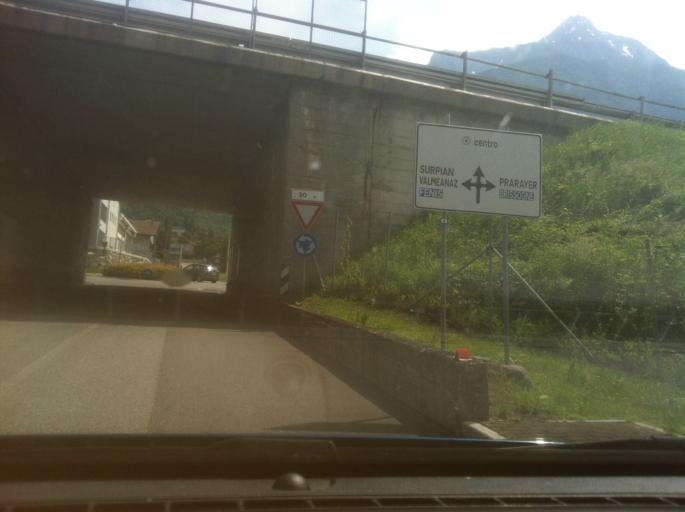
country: IT
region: Aosta Valley
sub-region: Valle d'Aosta
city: Saint Marcel
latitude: 45.7365
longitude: 7.4417
